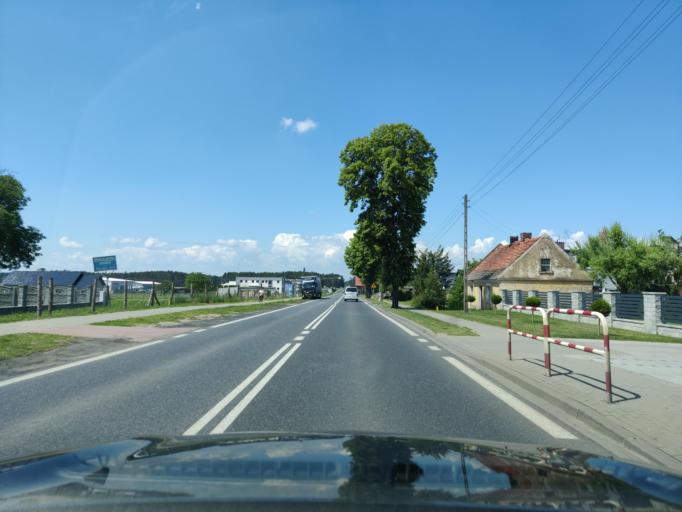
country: PL
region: Greater Poland Voivodeship
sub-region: Powiat grodziski
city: Jablonna
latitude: 52.1316
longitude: 16.1916
